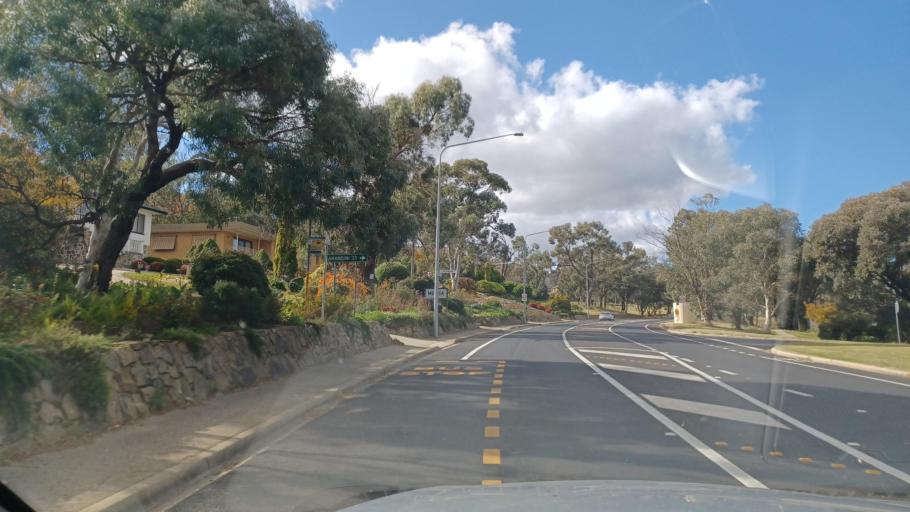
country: AU
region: Australian Capital Territory
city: Belconnen
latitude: -35.2036
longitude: 149.0513
